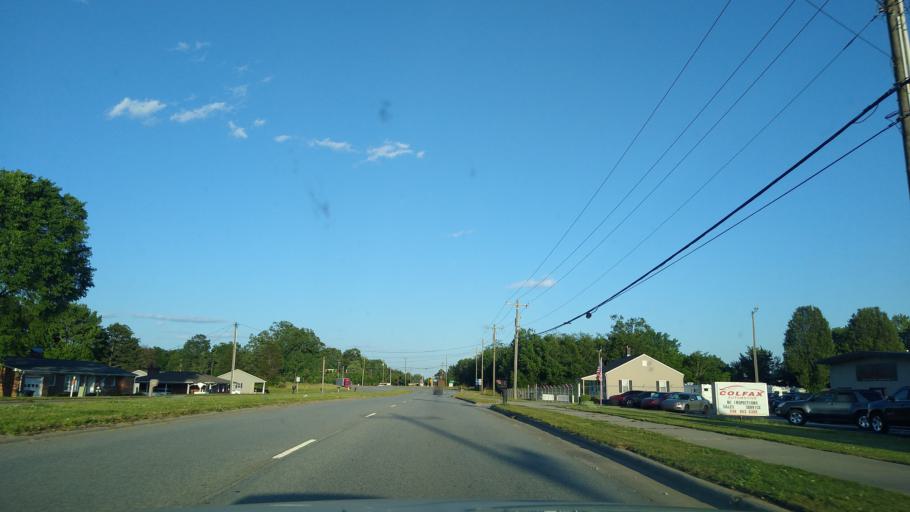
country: US
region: North Carolina
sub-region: Guilford County
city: Oak Ridge
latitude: 36.1030
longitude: -79.9998
